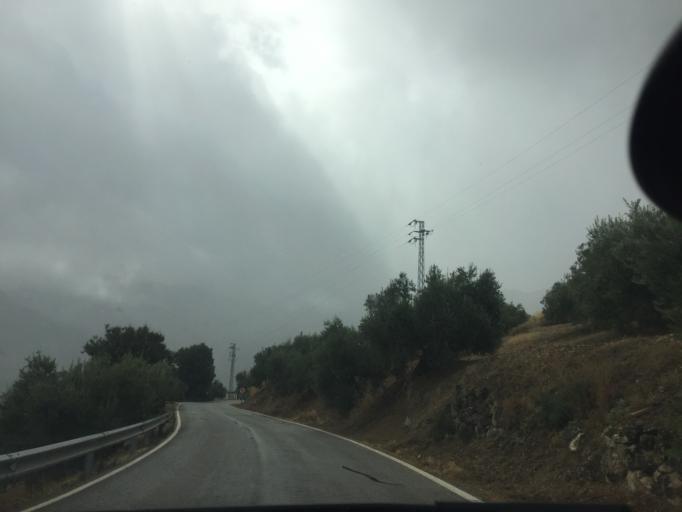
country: ES
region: Andalusia
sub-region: Provincia de Jaen
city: Jimena
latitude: 37.8097
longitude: -3.4589
